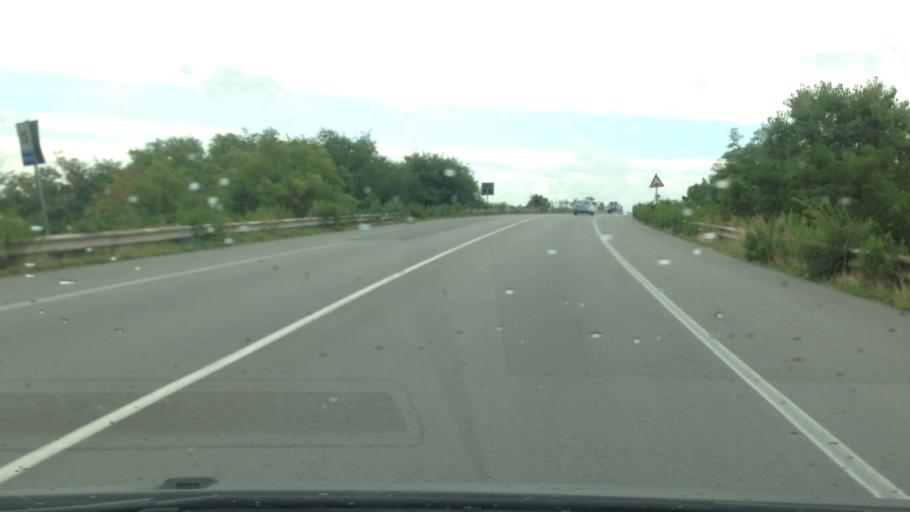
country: IT
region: Piedmont
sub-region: Provincia di Alessandria
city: Tortona
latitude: 44.8979
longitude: 8.8399
